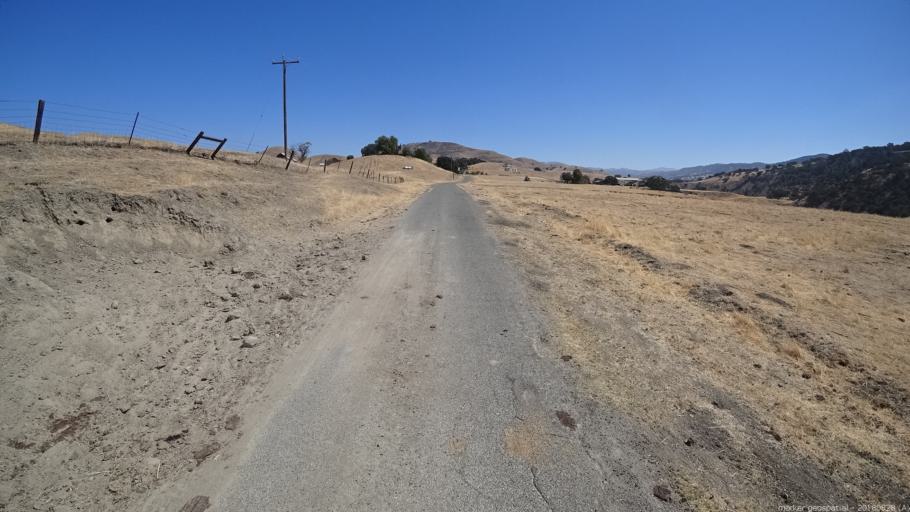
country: US
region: California
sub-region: San Luis Obispo County
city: San Miguel
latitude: 36.0656
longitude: -120.7855
